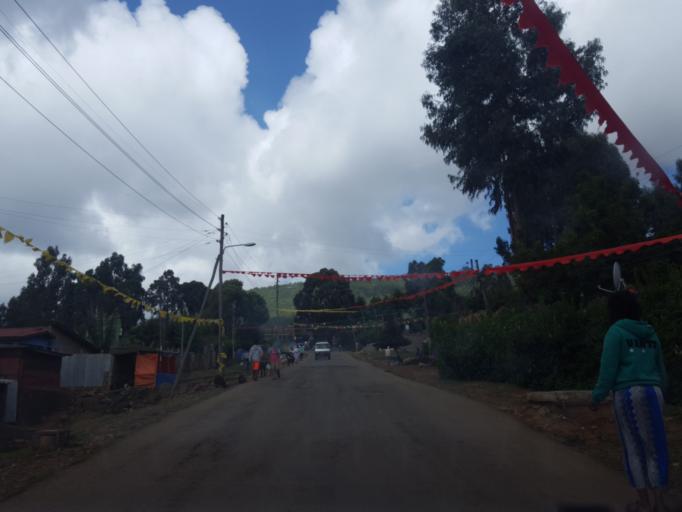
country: ET
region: Adis Abeba
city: Addis Ababa
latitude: 9.0766
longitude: 38.7585
